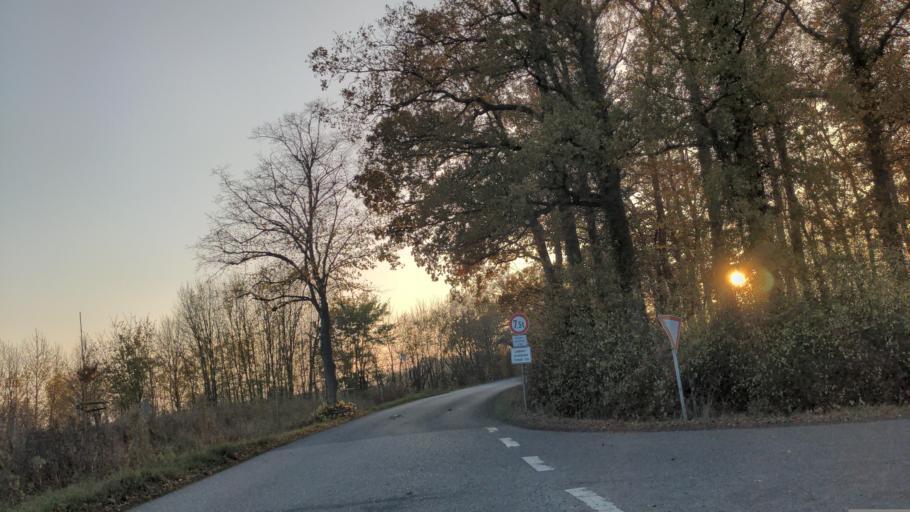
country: DE
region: Schleswig-Holstein
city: Glasau
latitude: 54.0924
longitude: 10.5118
